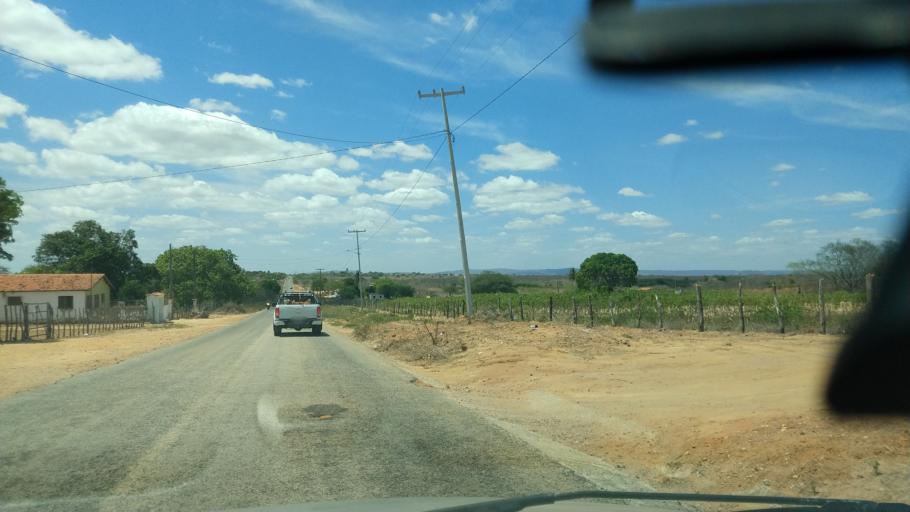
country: BR
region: Rio Grande do Norte
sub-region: Sao Paulo Do Potengi
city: Sao Paulo do Potengi
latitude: -5.9156
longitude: -35.7300
